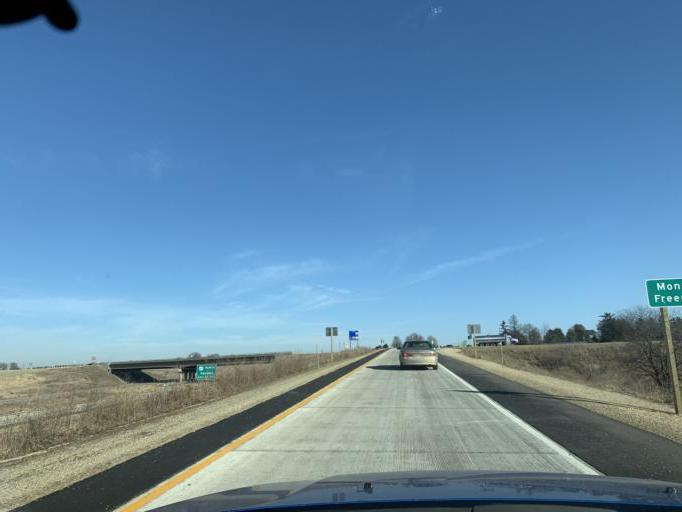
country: US
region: Wisconsin
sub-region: Green County
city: Monroe
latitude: 42.6120
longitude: -89.6542
